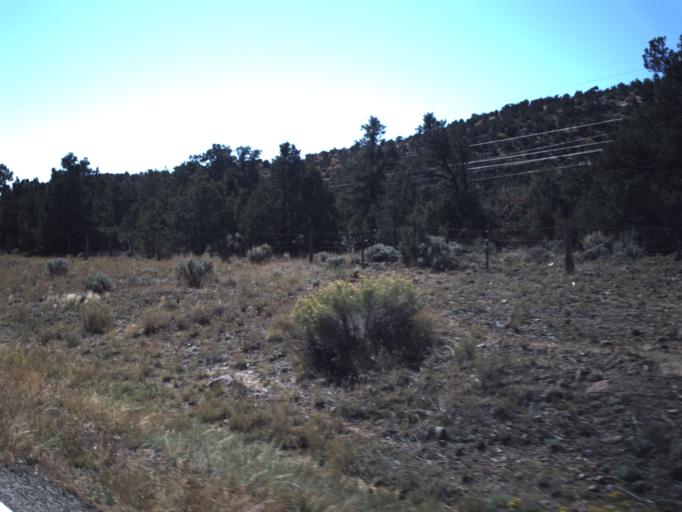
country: US
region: Utah
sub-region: Wayne County
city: Loa
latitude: 37.9266
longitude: -111.4274
